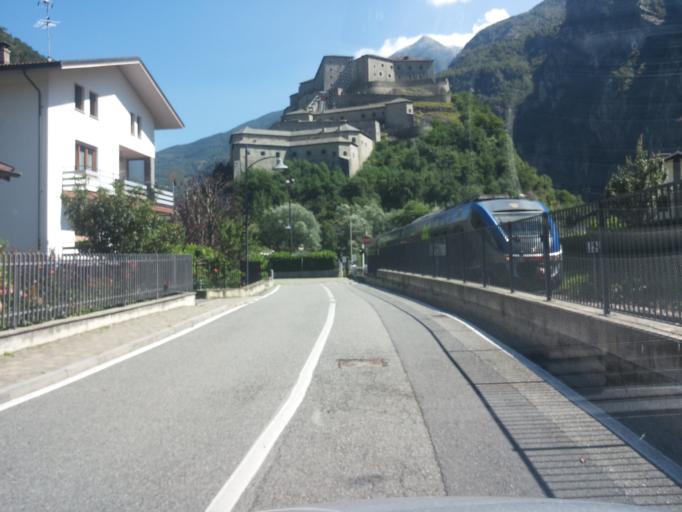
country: IT
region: Aosta Valley
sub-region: Valle d'Aosta
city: Bard
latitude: 45.6120
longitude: 7.7427
